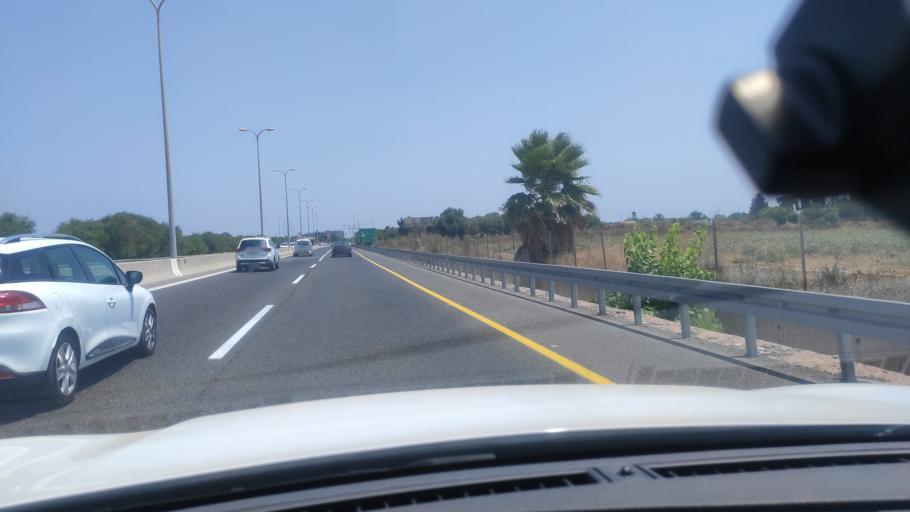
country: IL
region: Central District
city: Hod HaSharon
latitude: 32.1478
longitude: 34.9192
